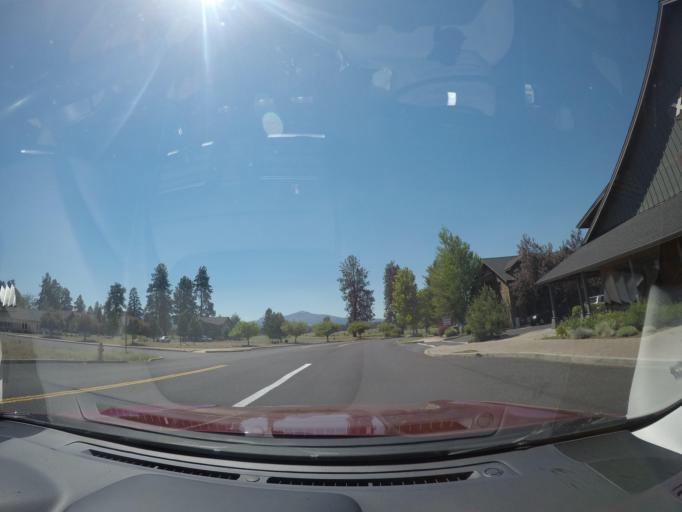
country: US
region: Oregon
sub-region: Deschutes County
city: Sisters
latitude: 44.2906
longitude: -121.5573
